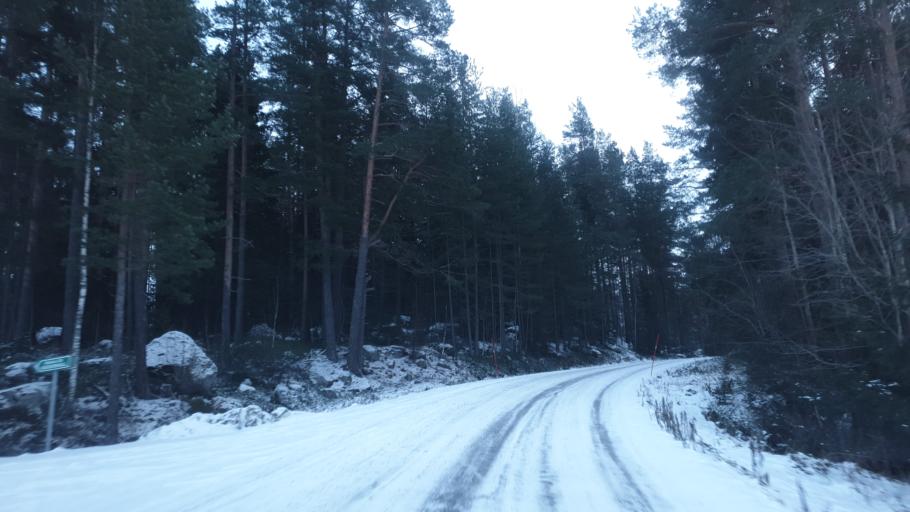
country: SE
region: Gaevleborg
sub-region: Bollnas Kommun
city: Kilafors
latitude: 61.2556
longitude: 16.5408
